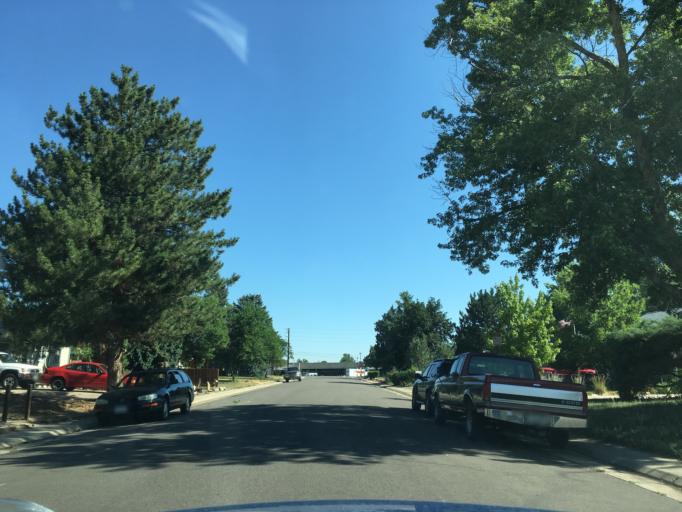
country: US
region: Colorado
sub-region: Jefferson County
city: Lakewood
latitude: 39.6882
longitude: -105.0521
